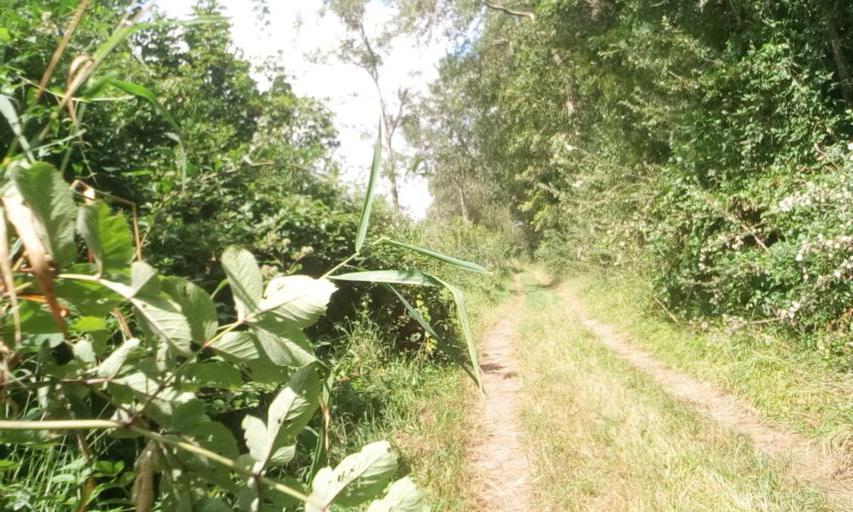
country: FR
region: Lower Normandy
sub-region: Departement du Calvados
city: Bellengreville
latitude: 49.1542
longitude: -0.2058
